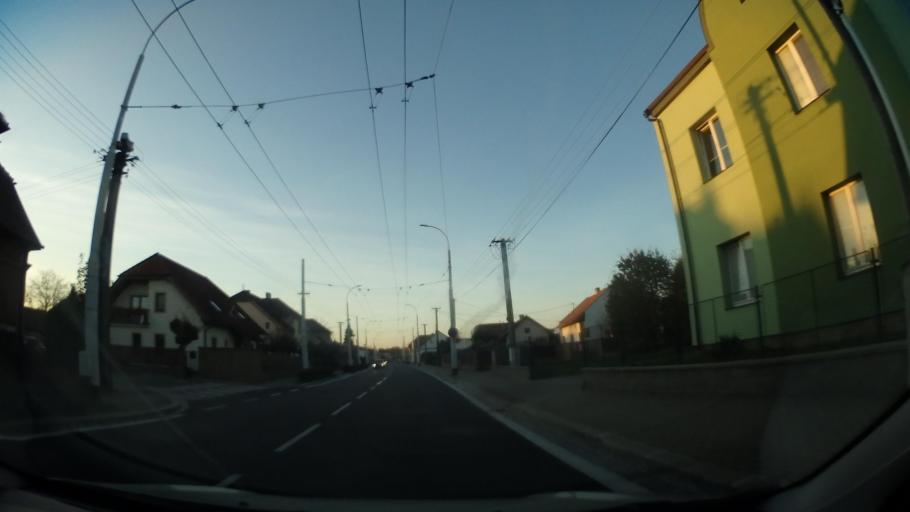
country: CZ
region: Pardubicky
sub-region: Okres Pardubice
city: Lazne Bohdanec
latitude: 50.0783
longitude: 15.6767
